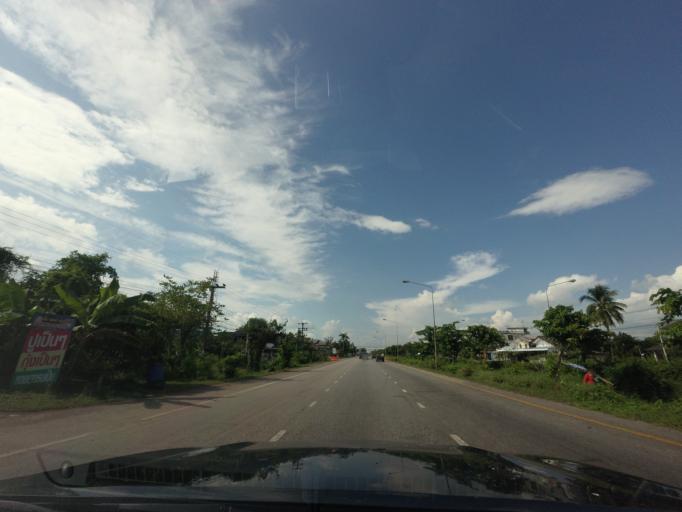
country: TH
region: Nong Khai
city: Sa Khrai
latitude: 17.6845
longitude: 102.7839
